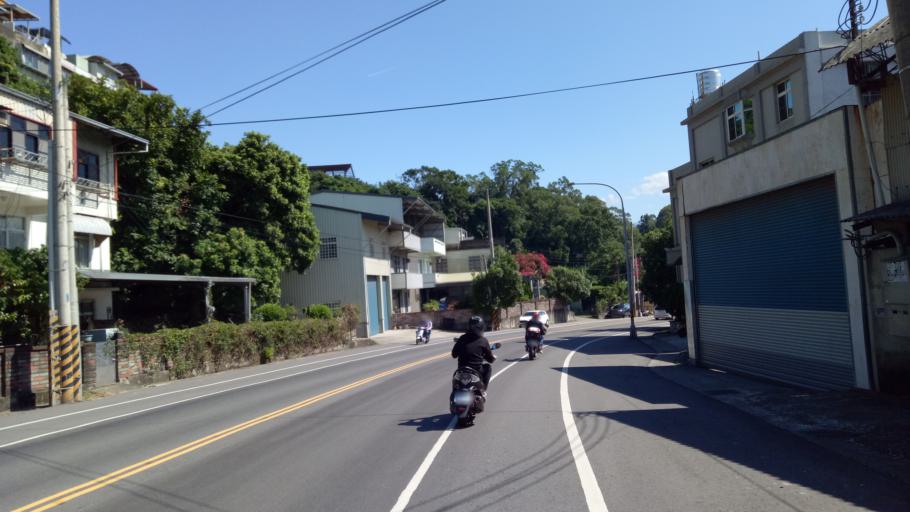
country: TW
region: Taiwan
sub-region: Hsinchu
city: Hsinchu
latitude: 24.6841
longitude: 120.9618
